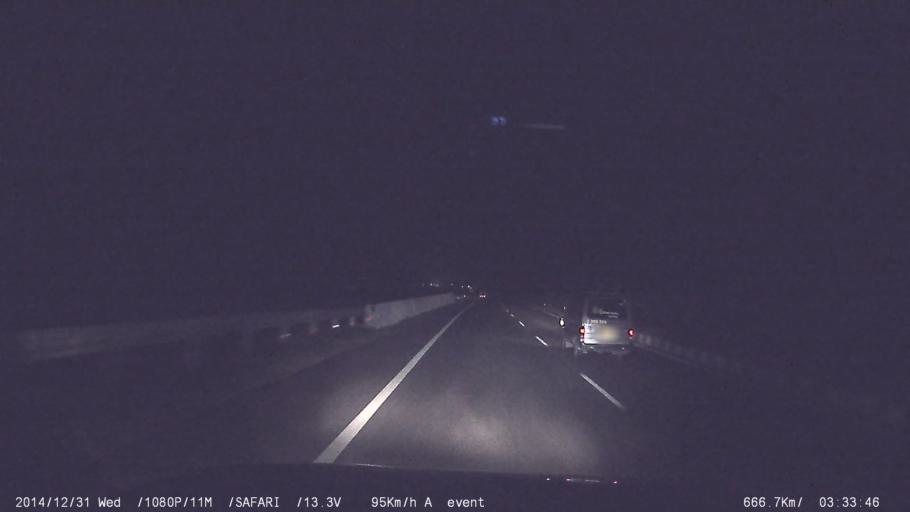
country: IN
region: Tamil Nadu
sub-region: Salem
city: Belur
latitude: 11.6547
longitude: 78.4392
